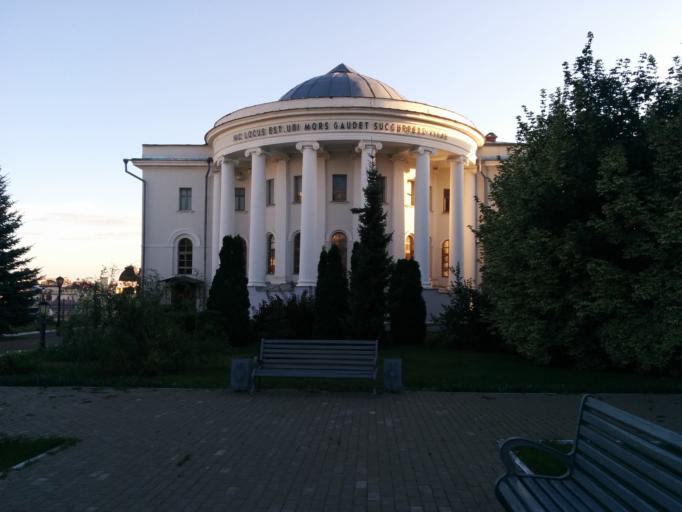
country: RU
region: Tatarstan
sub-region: Gorod Kazan'
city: Kazan
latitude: 55.7903
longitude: 49.1211
